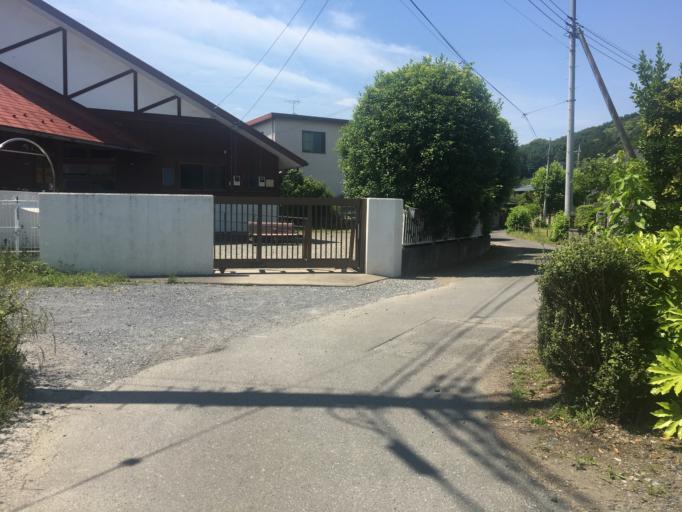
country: JP
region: Saitama
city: Ogawa
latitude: 36.0028
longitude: 139.2757
